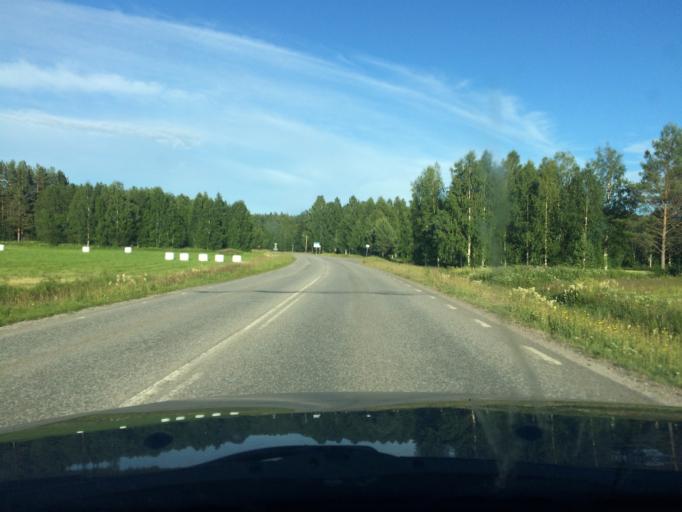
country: SE
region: Norrbotten
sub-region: Pitea Kommun
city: Roknas
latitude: 65.3184
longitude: 21.2448
